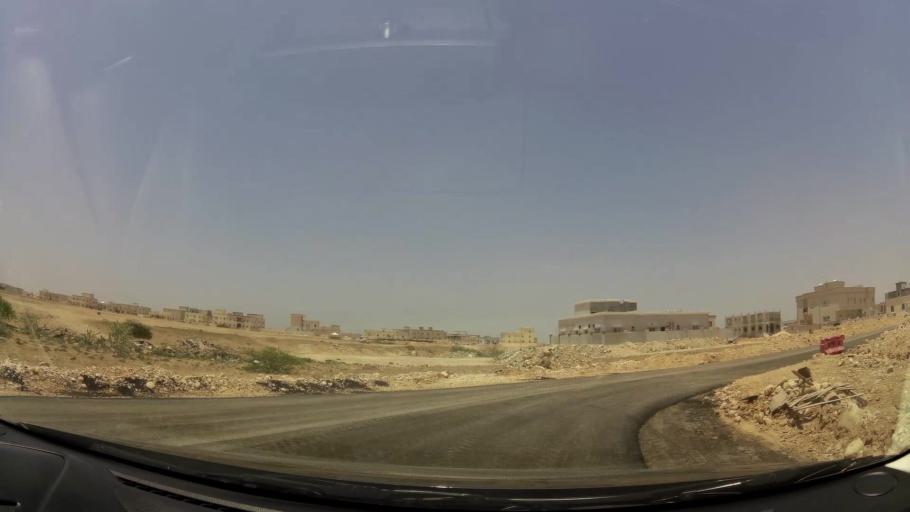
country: OM
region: Zufar
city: Salalah
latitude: 17.0959
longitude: 54.1634
